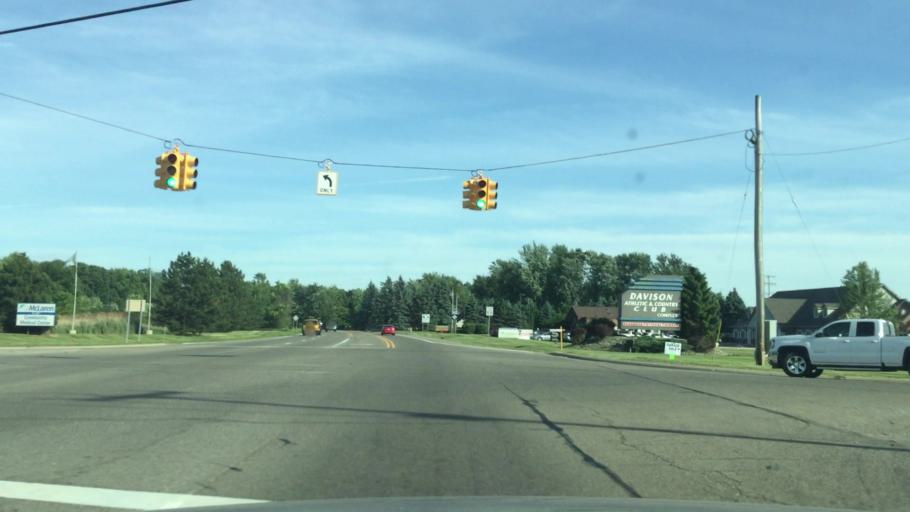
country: US
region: Michigan
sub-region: Genesee County
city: Davison
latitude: 43.0056
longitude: -83.5161
